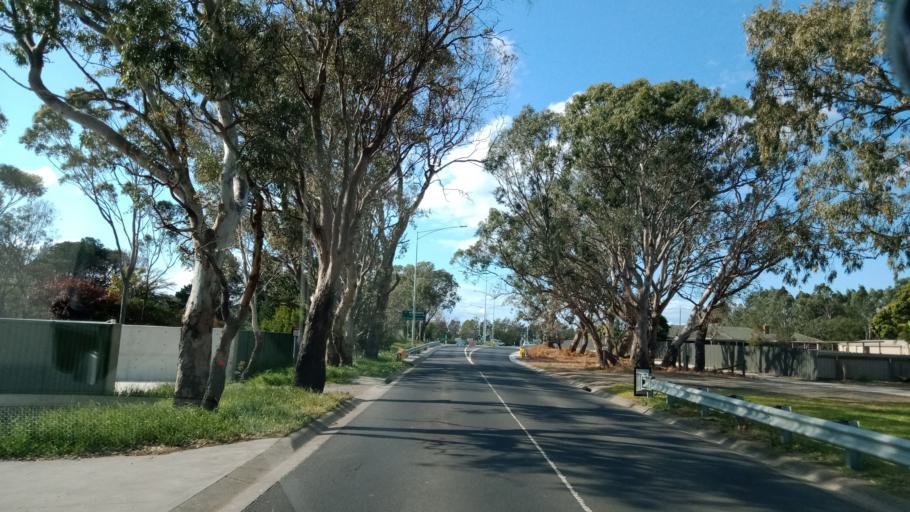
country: AU
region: Victoria
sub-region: Frankston
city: Sandhurst
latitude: -38.0752
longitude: 145.2027
